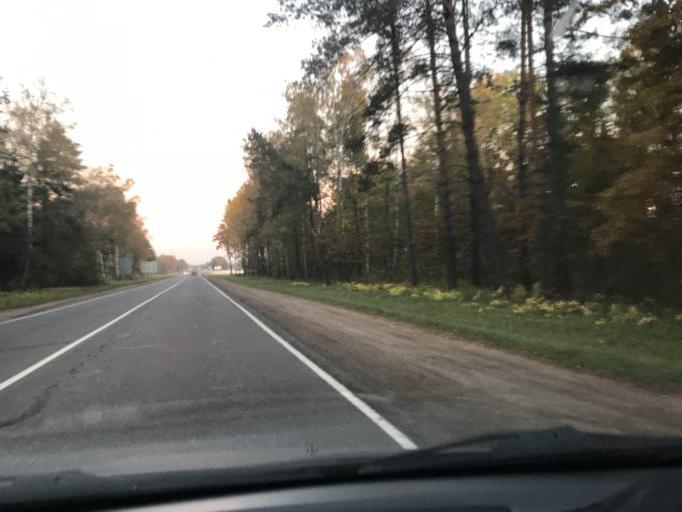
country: BY
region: Mogilev
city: Babruysk
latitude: 53.2084
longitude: 29.0808
